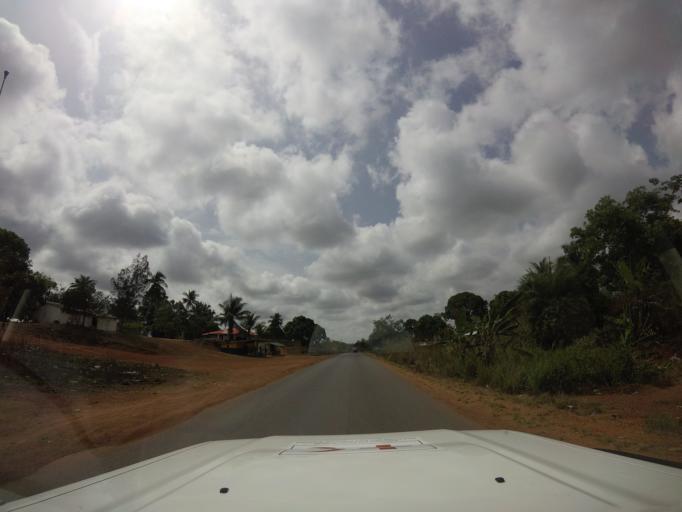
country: LR
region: Montserrado
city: Monrovia
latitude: 6.4758
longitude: -10.8110
